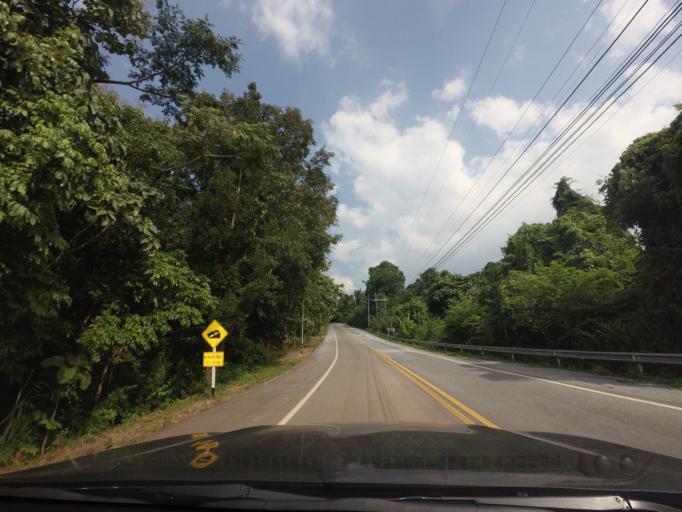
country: TH
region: Phitsanulok
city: Nakhon Thai
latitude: 17.0226
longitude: 100.9378
